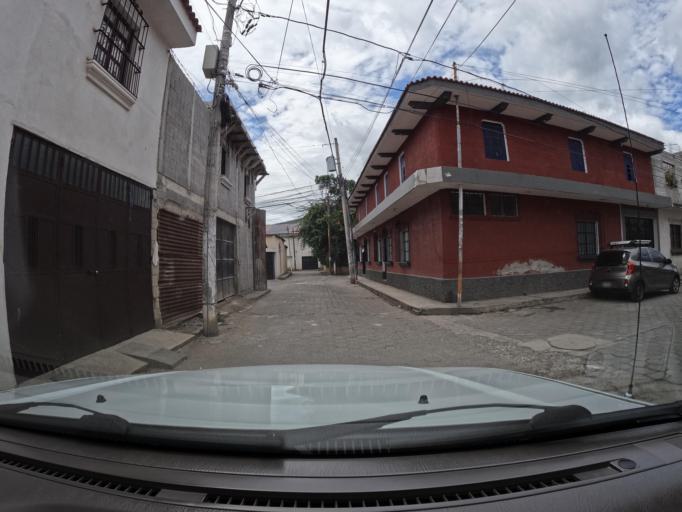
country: GT
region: Sacatepequez
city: Jocotenango
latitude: 14.5729
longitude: -90.7397
